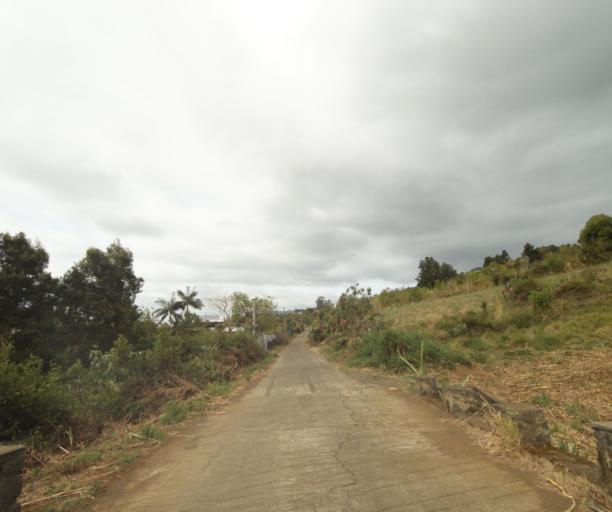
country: RE
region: Reunion
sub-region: Reunion
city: Saint-Paul
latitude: -21.0185
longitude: 55.3267
